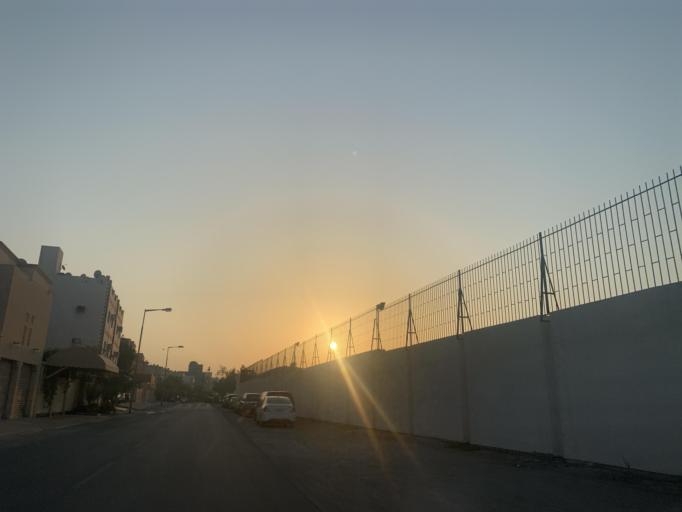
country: BH
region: Manama
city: Jidd Hafs
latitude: 26.2166
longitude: 50.5283
